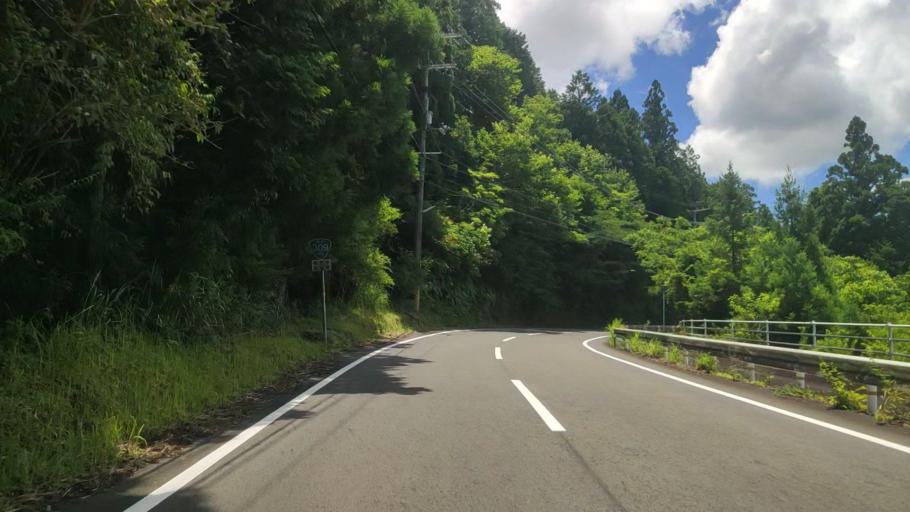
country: JP
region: Mie
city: Owase
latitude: 33.9535
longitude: 136.0689
